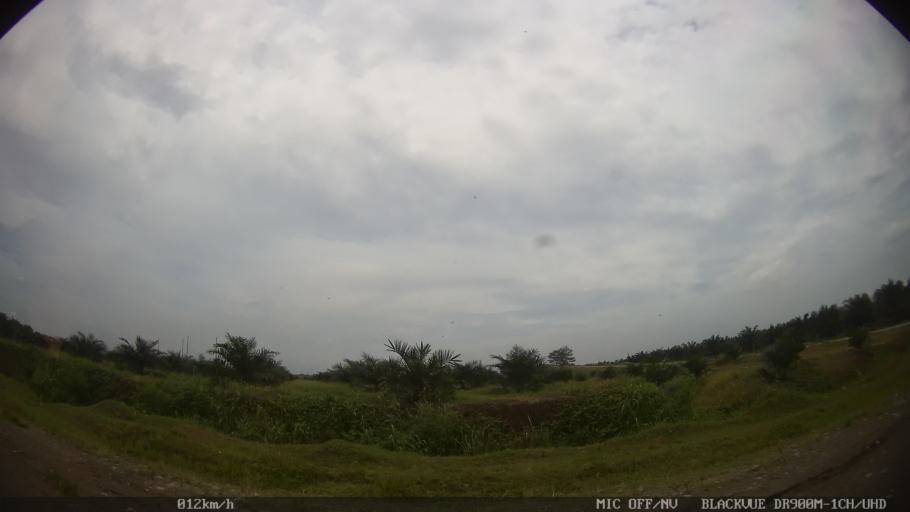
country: ID
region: North Sumatra
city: Sunggal
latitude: 3.6344
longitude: 98.5839
